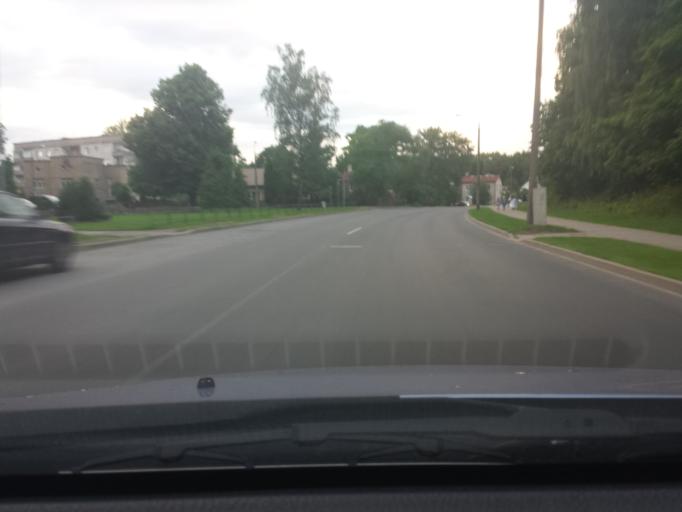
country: LV
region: Stopini
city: Ulbroka
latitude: 56.9724
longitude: 24.2414
